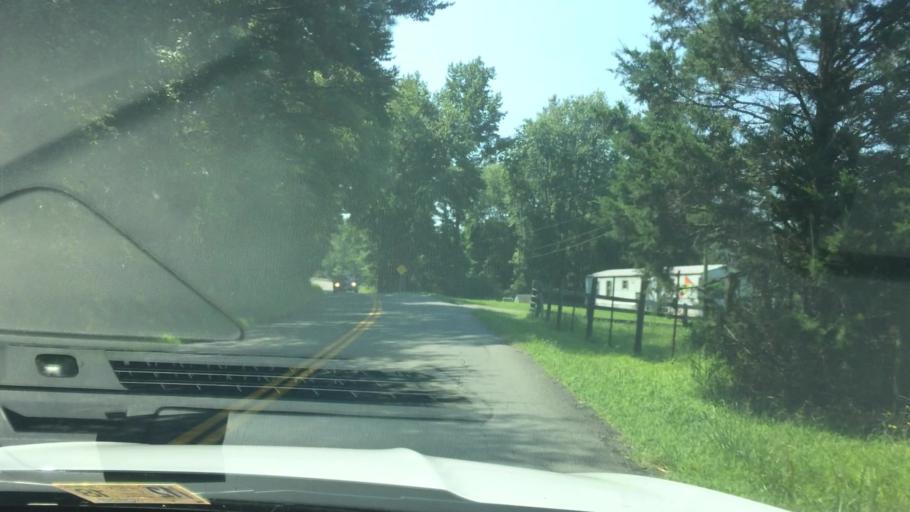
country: US
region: Virginia
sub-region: Henrico County
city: Sandston
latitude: 37.5163
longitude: -77.1616
